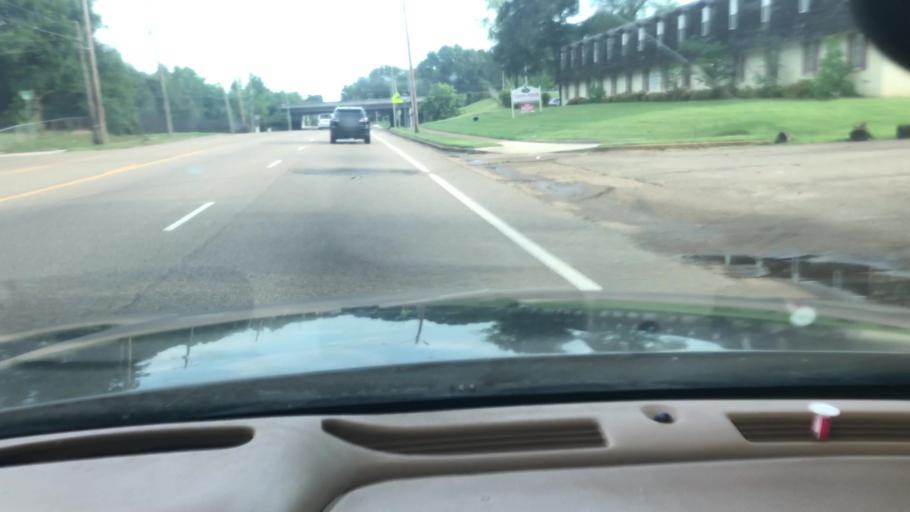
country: US
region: Mississippi
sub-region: De Soto County
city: Southaven
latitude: 35.0477
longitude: -90.0076
